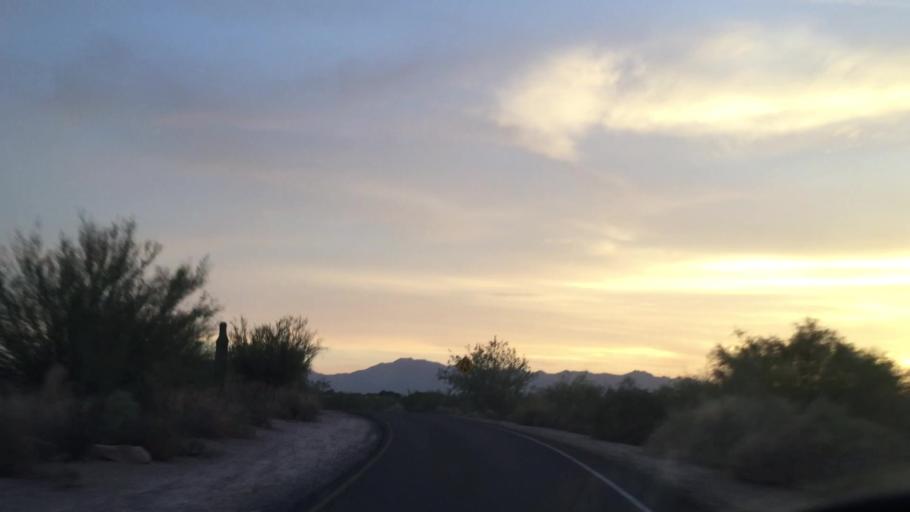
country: US
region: Arizona
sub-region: Maricopa County
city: Guadalupe
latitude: 33.2765
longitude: -111.9804
